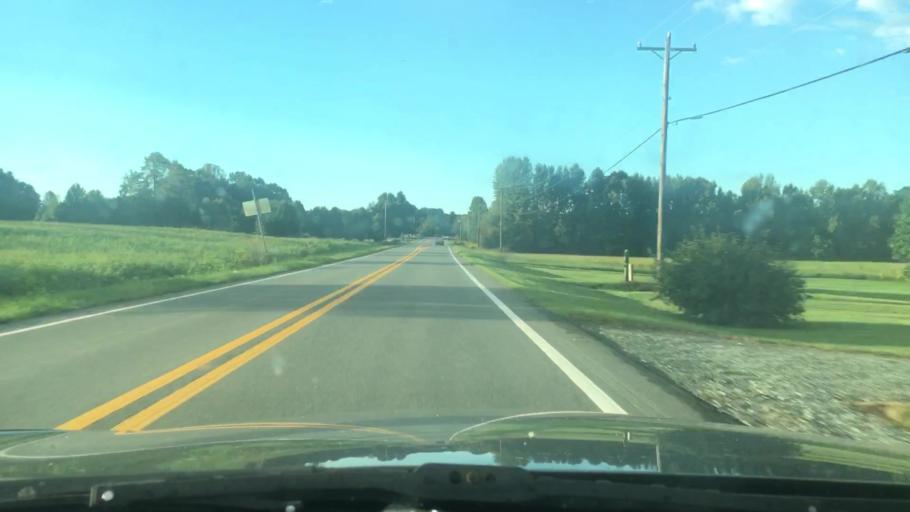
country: US
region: North Carolina
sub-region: Alamance County
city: Green Level
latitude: 36.2024
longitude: -79.3225
